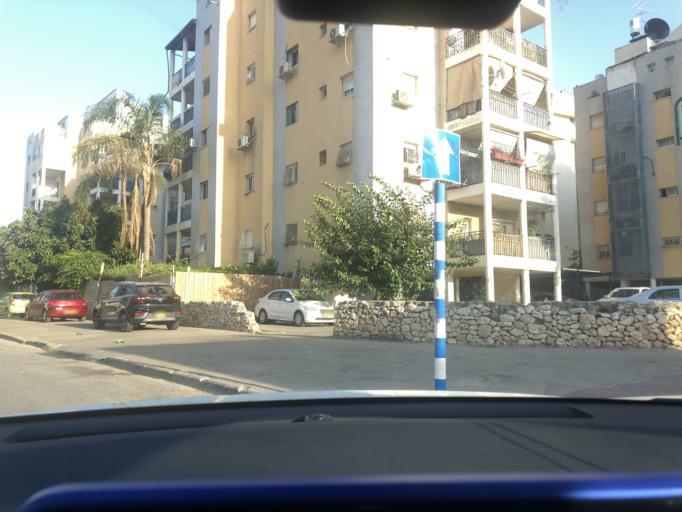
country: IL
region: Central District
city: Lod
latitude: 31.9537
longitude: 34.8962
